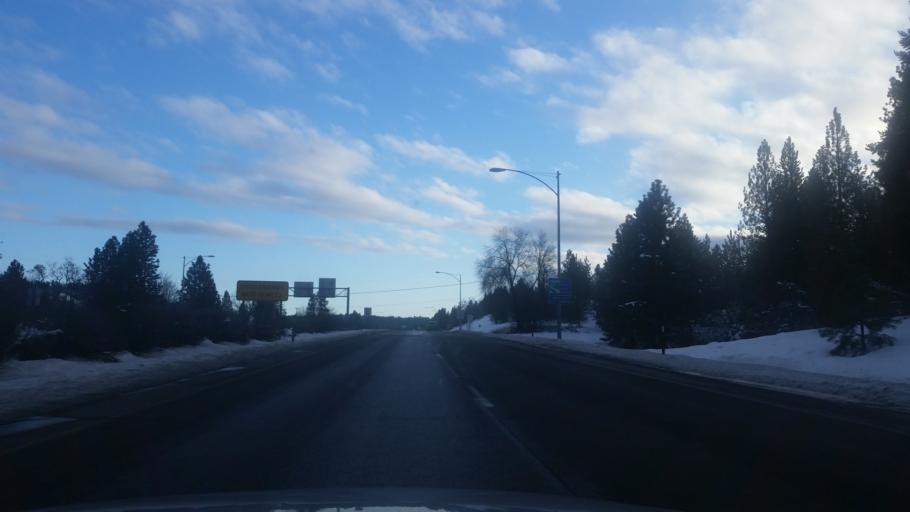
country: US
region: Washington
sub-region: Spokane County
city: Spokane
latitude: 47.6449
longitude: -117.4502
